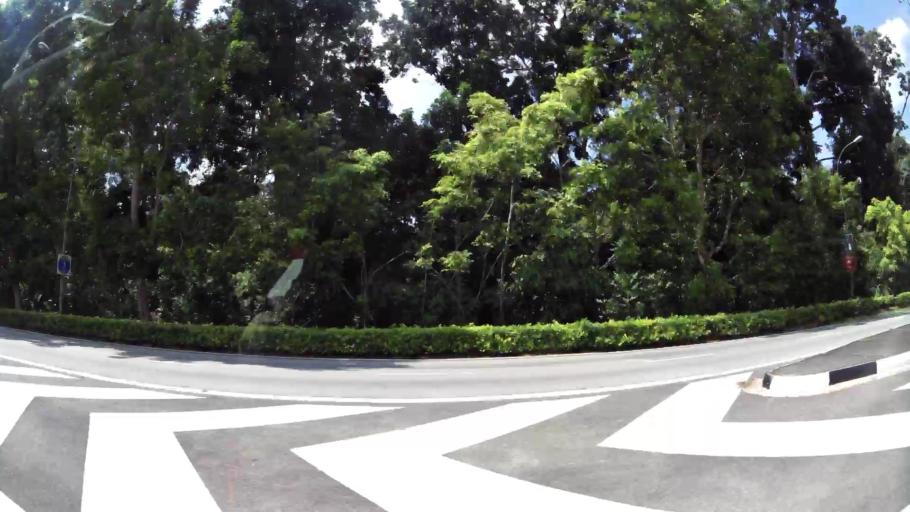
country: SG
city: Singapore
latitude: 1.3626
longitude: 103.7800
